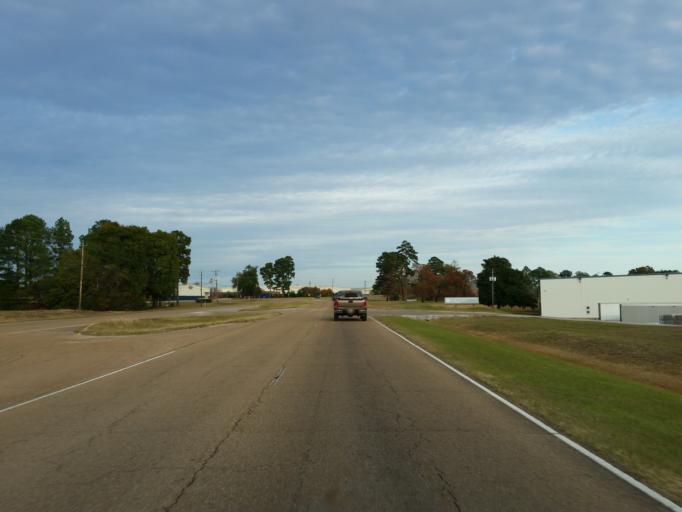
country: US
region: Mississippi
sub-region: Lauderdale County
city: Marion
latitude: 32.4113
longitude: -88.6262
